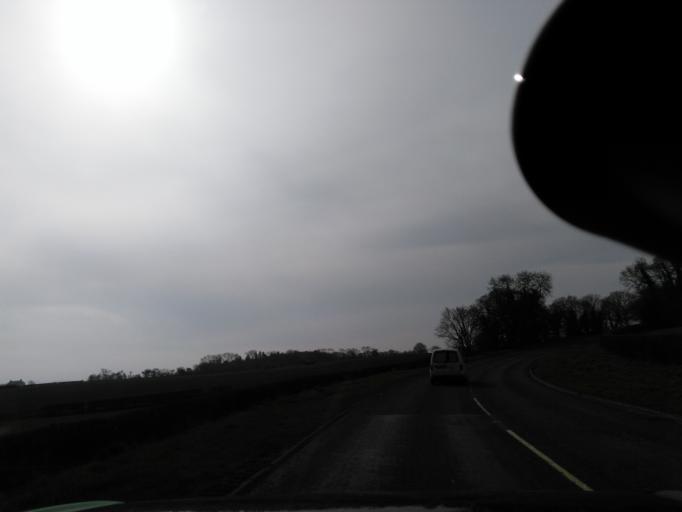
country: GB
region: England
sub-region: North Yorkshire
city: Northallerton
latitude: 54.2995
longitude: -1.3928
